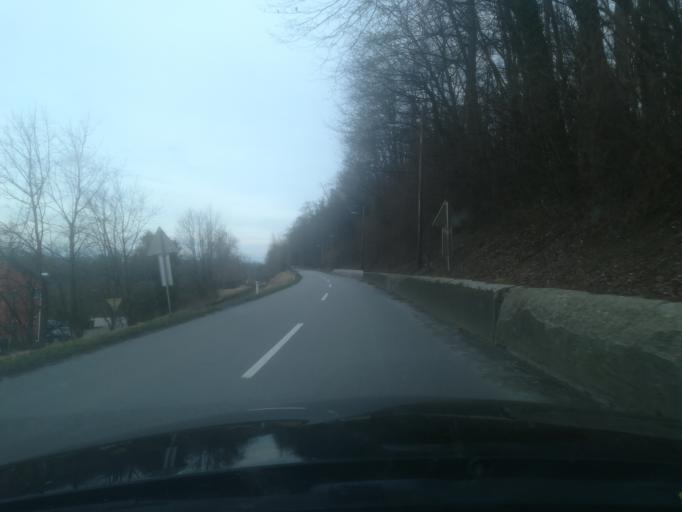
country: AT
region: Upper Austria
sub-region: Wels-Land
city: Thalheim bei Wels
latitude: 48.1422
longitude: 14.0129
